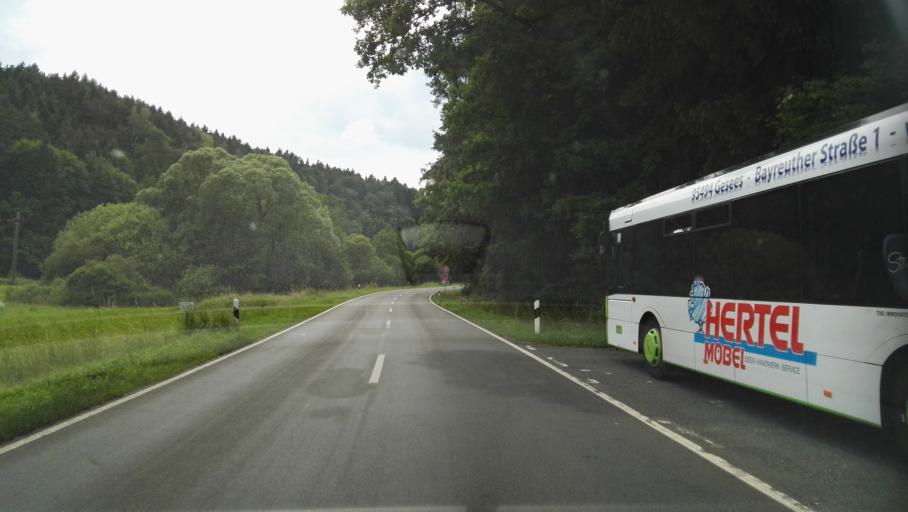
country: DE
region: Bavaria
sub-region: Upper Franconia
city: Plankenfels
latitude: 49.8775
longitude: 11.3408
